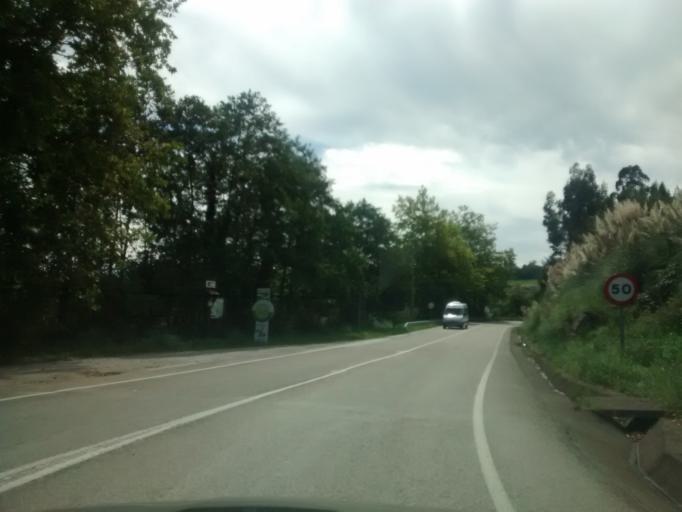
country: ES
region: Cantabria
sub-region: Provincia de Cantabria
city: Miengo
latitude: 43.4147
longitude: -3.9592
